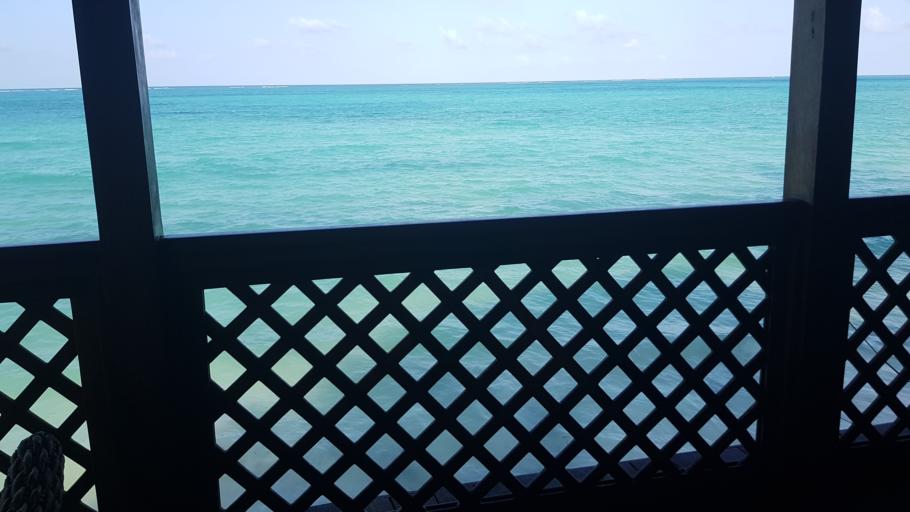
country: TZ
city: Kiwengwa
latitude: -6.0347
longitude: 39.4074
